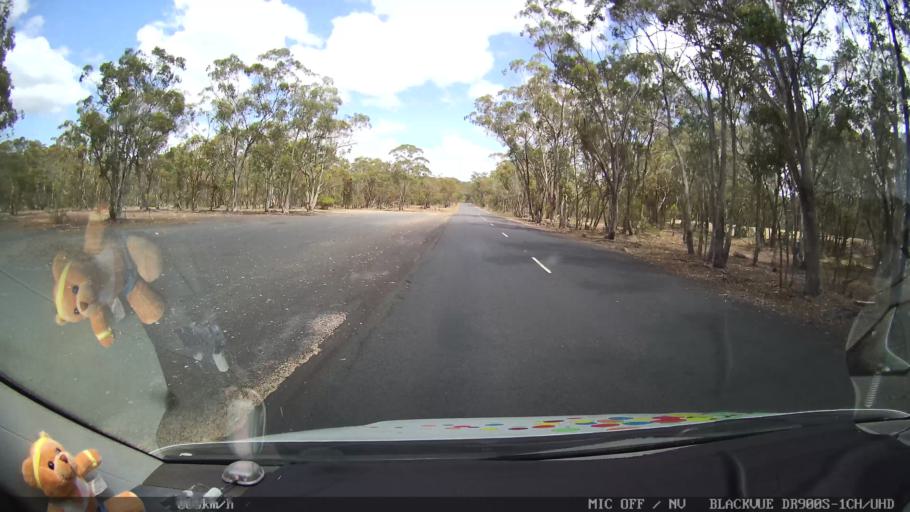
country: AU
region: New South Wales
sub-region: Glen Innes Severn
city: Glen Innes
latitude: -29.4615
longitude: 151.6167
